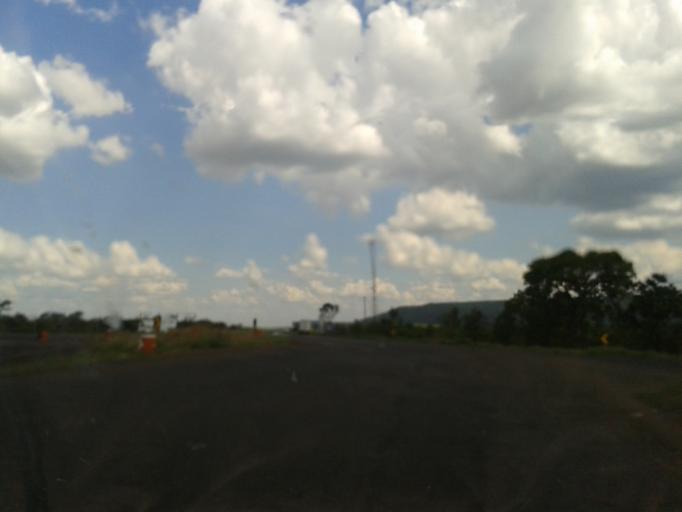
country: BR
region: Goias
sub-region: Caldas Novas
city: Caldas Novas
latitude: -17.6988
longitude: -48.7097
